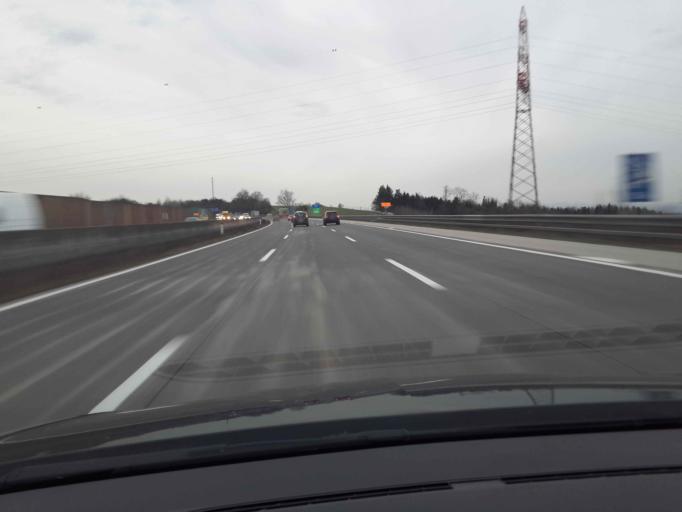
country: AT
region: Lower Austria
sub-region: Politischer Bezirk Amstetten
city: Strengberg
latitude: 48.1266
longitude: 14.6098
